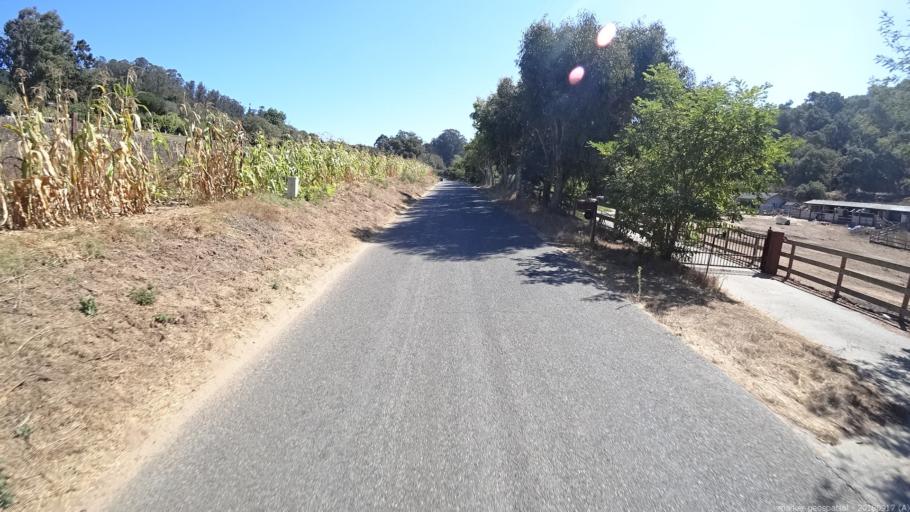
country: US
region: California
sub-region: Monterey County
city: Elkhorn
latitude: 36.8250
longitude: -121.7048
